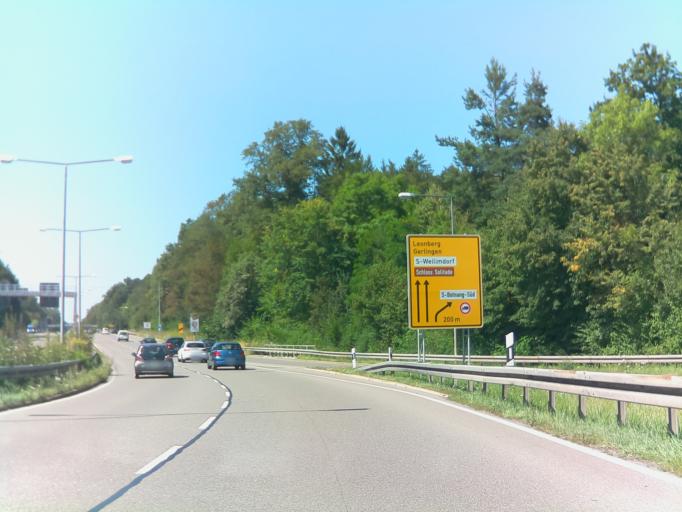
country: DE
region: Baden-Wuerttemberg
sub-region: Regierungsbezirk Stuttgart
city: Stuttgart Feuerbach
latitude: 48.7650
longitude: 9.1161
